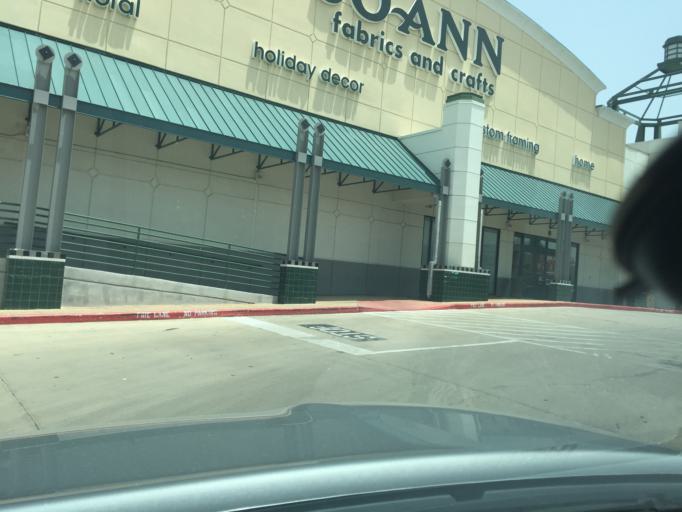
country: US
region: Texas
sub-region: Bexar County
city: Castle Hills
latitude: 29.5220
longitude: -98.4937
